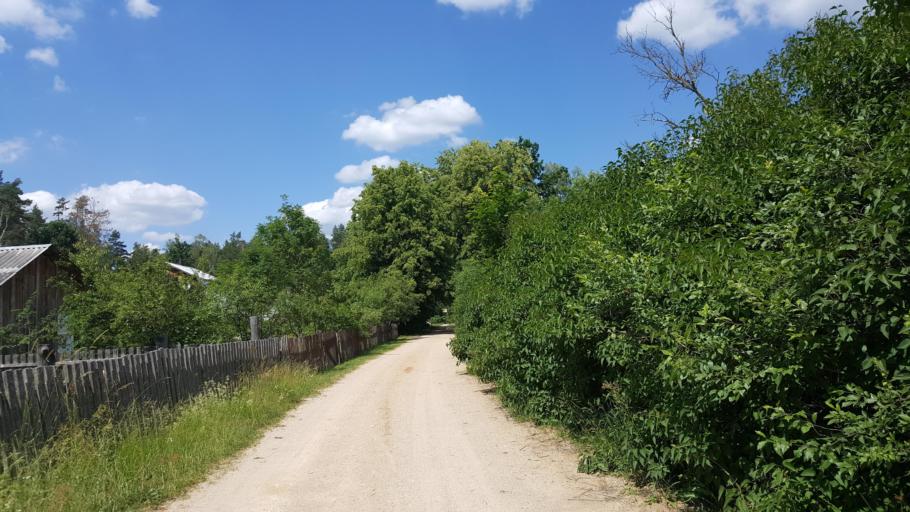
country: BY
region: Brest
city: Kamyanyuki
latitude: 52.5810
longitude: 23.7322
